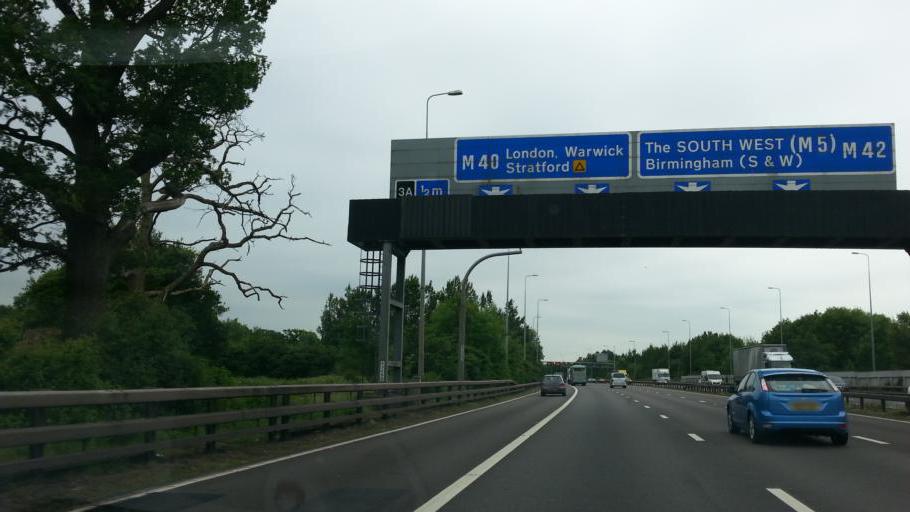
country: GB
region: England
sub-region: Solihull
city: Cheswick Green
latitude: 52.3638
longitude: -1.8030
